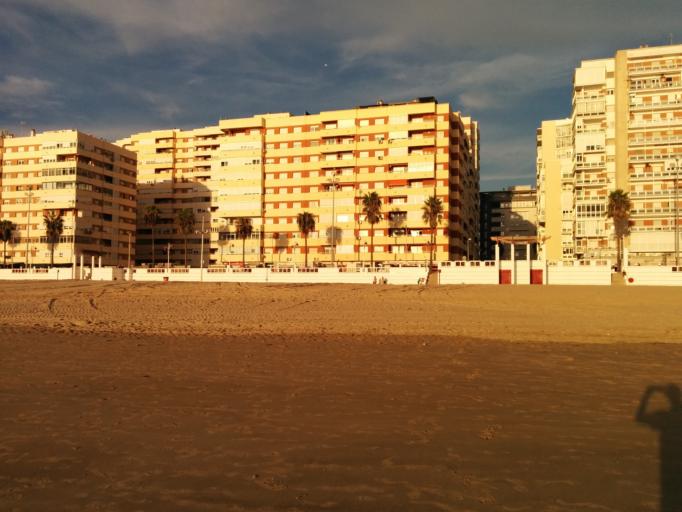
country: ES
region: Andalusia
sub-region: Provincia de Cadiz
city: Cadiz
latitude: 36.4978
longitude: -6.2743
